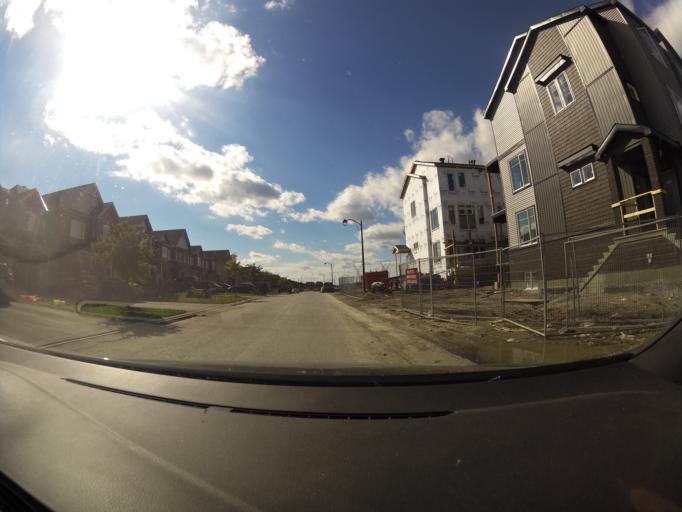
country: CA
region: Ontario
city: Bells Corners
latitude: 45.2764
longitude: -75.8886
